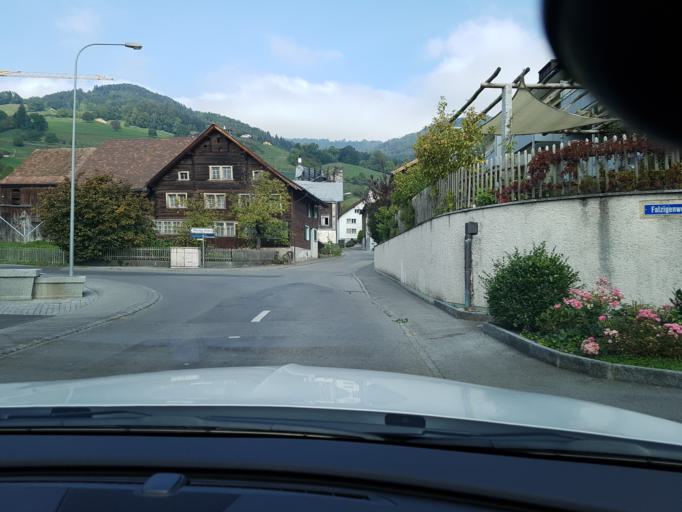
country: CH
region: Saint Gallen
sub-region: Wahlkreis Rheintal
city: Altstatten
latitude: 47.3890
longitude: 9.5556
